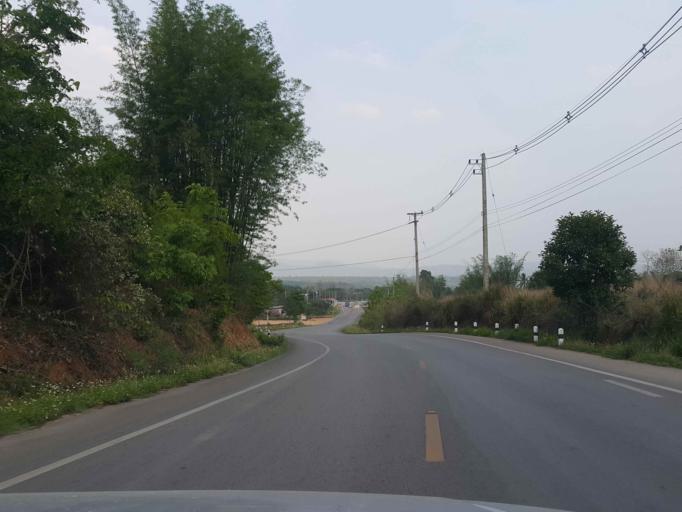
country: TH
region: Chiang Mai
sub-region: Amphoe Chiang Dao
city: Chiang Dao
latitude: 19.3536
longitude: 98.9568
